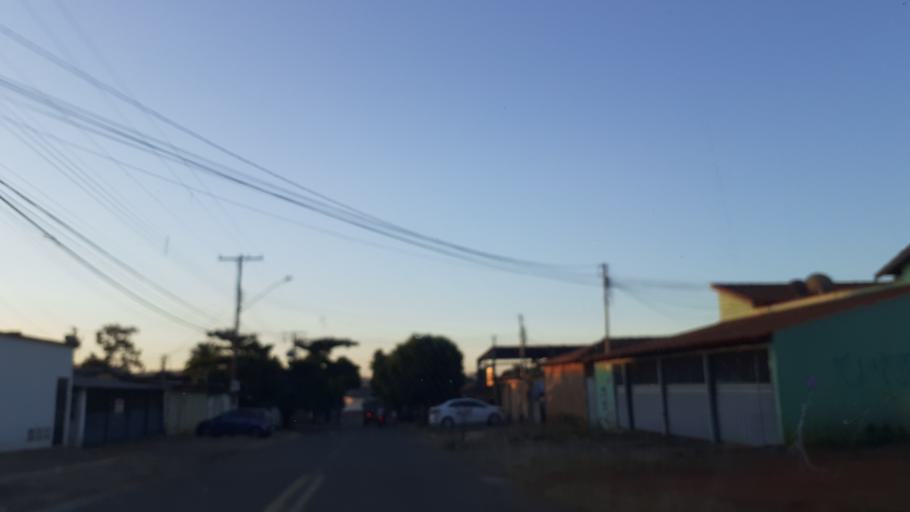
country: BR
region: Goias
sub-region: Goiania
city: Goiania
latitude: -16.7022
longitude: -49.3285
